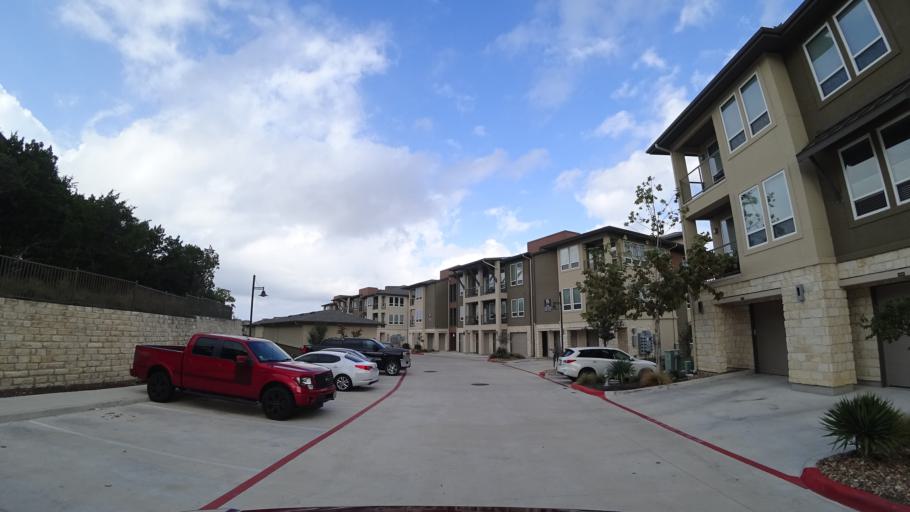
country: US
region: Texas
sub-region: Travis County
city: Hudson Bend
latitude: 30.3840
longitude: -97.8731
